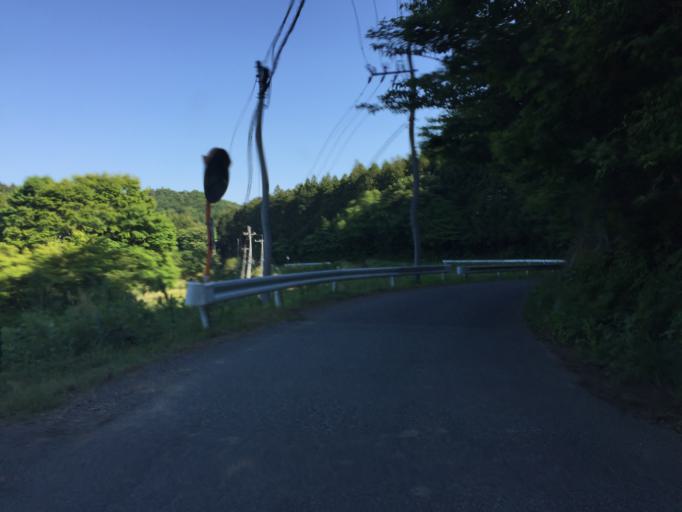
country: JP
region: Ibaraki
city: Kitaibaraki
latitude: 36.8721
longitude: 140.6560
